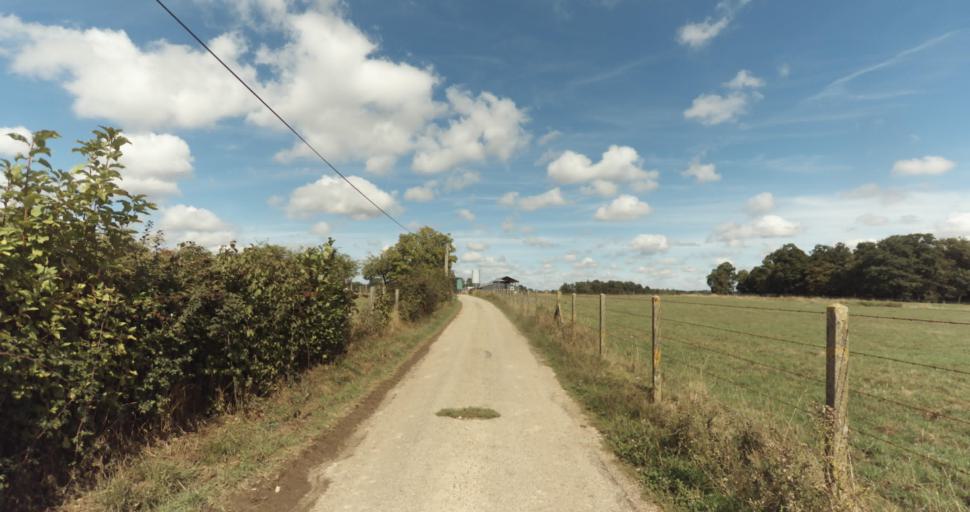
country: FR
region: Lower Normandy
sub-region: Departement du Calvados
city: Orbec
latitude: 48.9072
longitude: 0.3766
